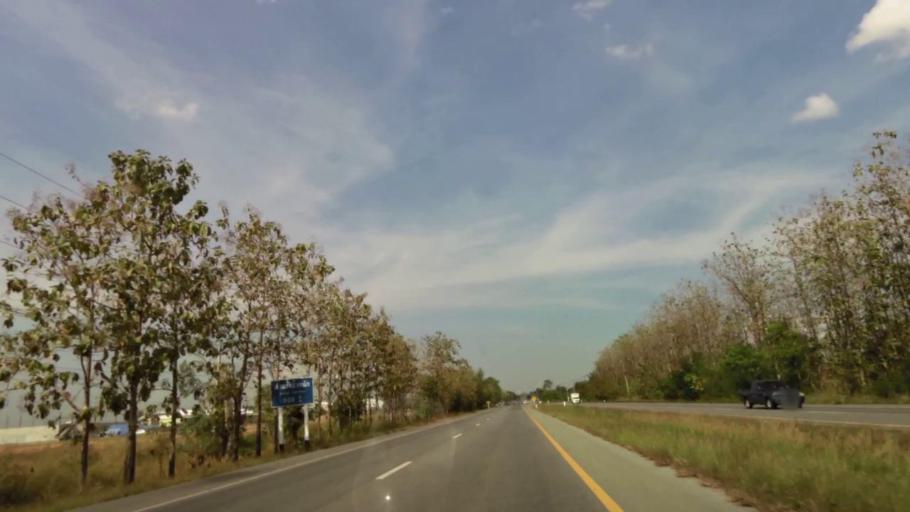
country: TH
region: Uttaradit
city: Tron
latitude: 17.5169
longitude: 100.2205
